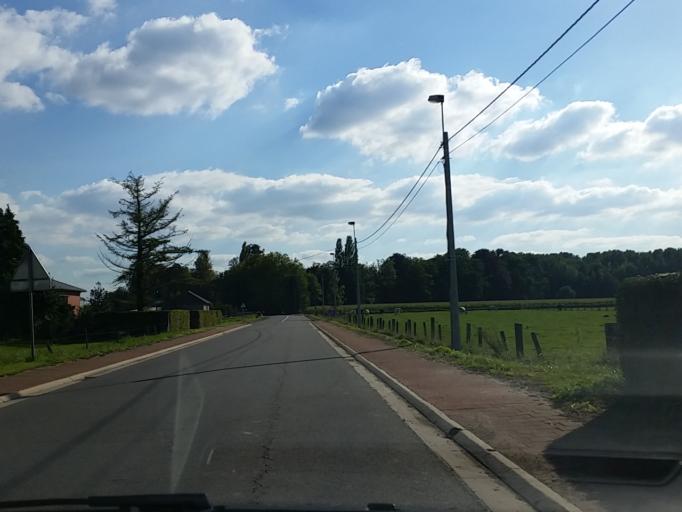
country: BE
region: Flanders
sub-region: Provincie Vlaams-Brabant
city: Haacht
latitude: 50.9324
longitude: 4.6163
